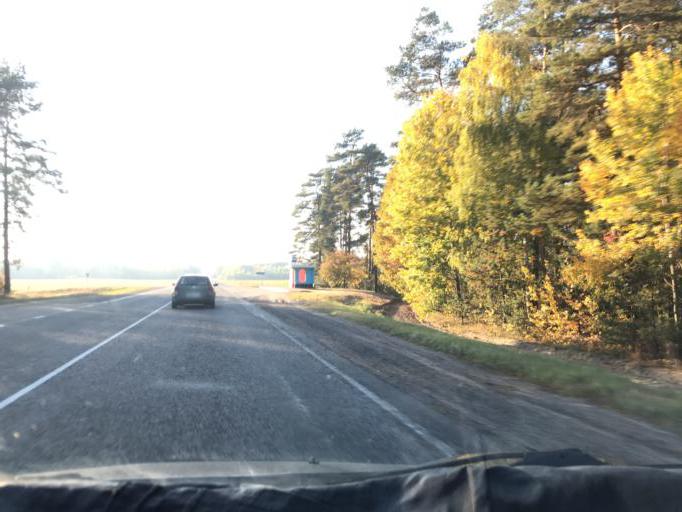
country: BY
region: Gomel
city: Zhytkavichy
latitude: 52.2727
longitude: 28.0281
